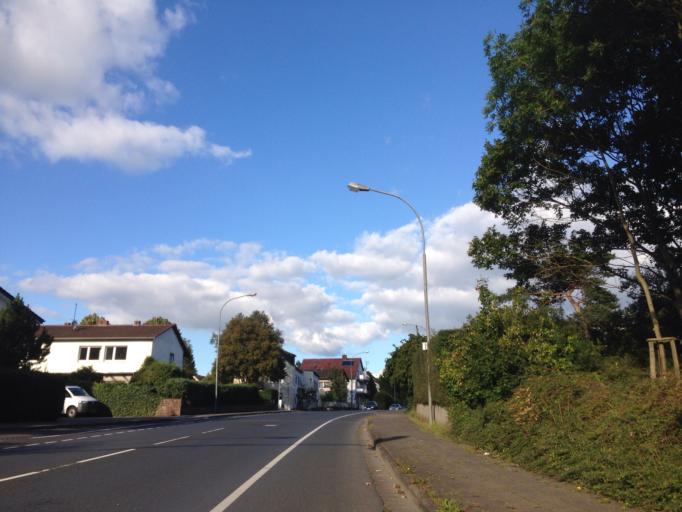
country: DE
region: Hesse
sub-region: Regierungsbezirk Giessen
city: Giessen
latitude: 50.5693
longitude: 8.6585
